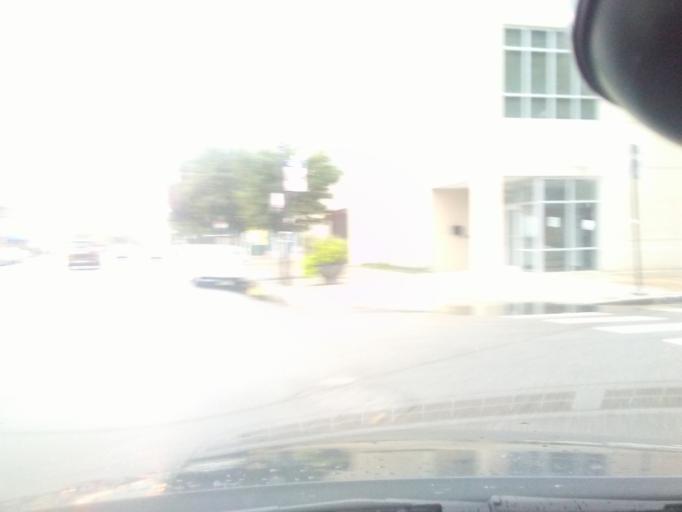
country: US
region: Illinois
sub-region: Cook County
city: Evanston
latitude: 41.9870
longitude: -87.6603
